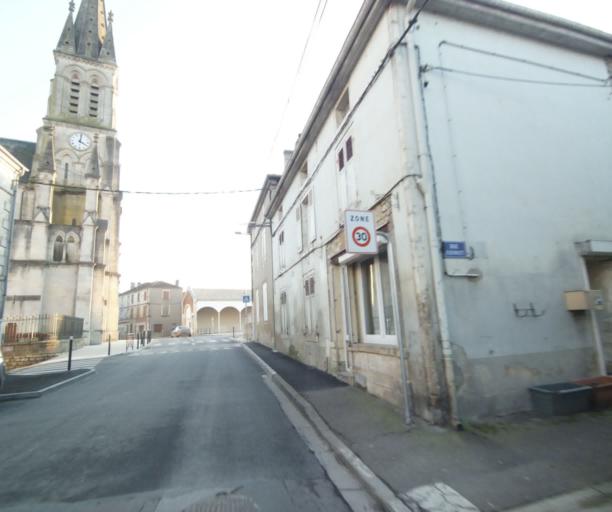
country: FR
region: Champagne-Ardenne
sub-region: Departement de la Haute-Marne
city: Bienville
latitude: 48.5855
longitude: 5.0371
